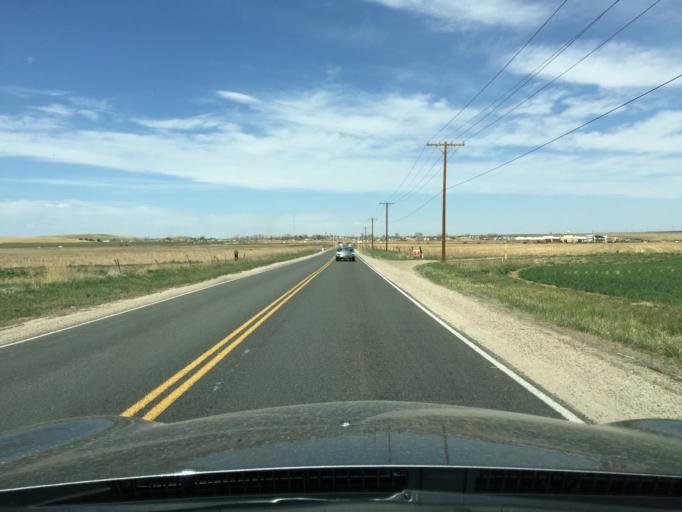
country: US
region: Colorado
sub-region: Boulder County
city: Erie
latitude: 39.9931
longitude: -104.9972
